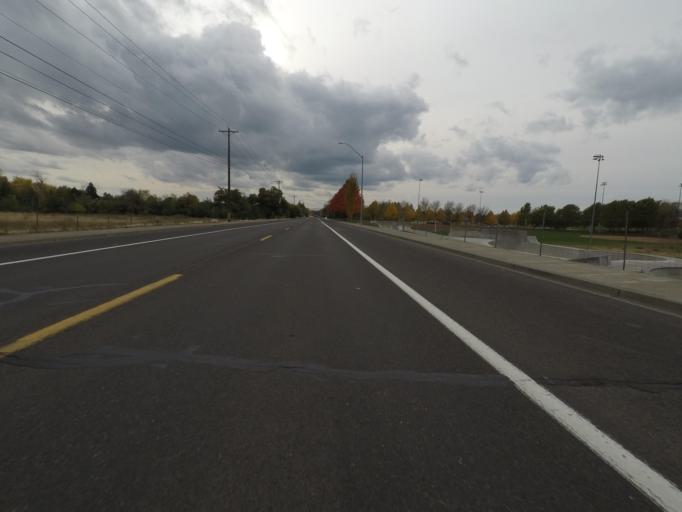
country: US
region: Washington
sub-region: Walla Walla County
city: Walla Walla East
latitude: 46.0734
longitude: -118.2862
